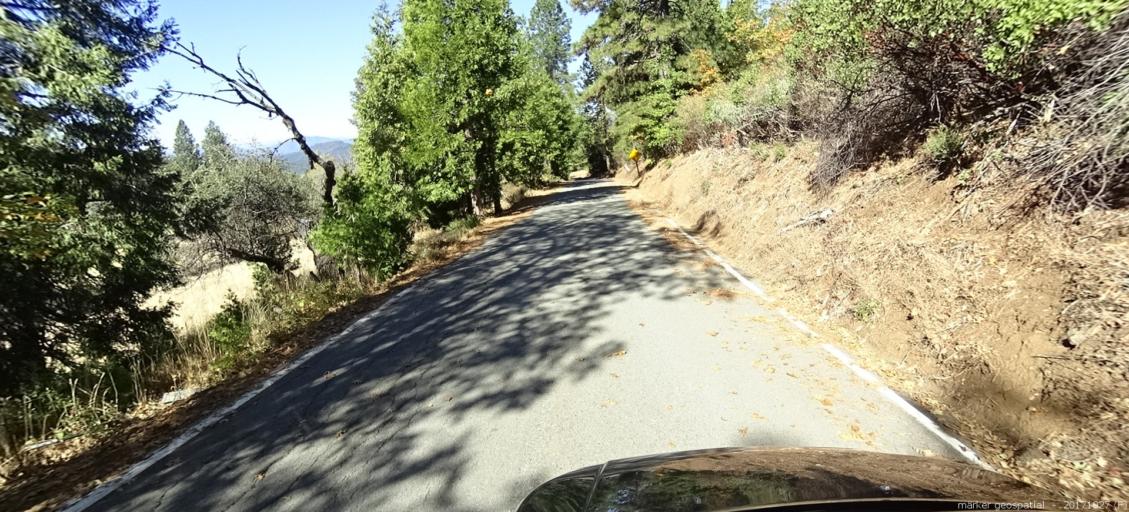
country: US
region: California
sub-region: Shasta County
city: Burney
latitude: 40.8050
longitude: -121.8995
